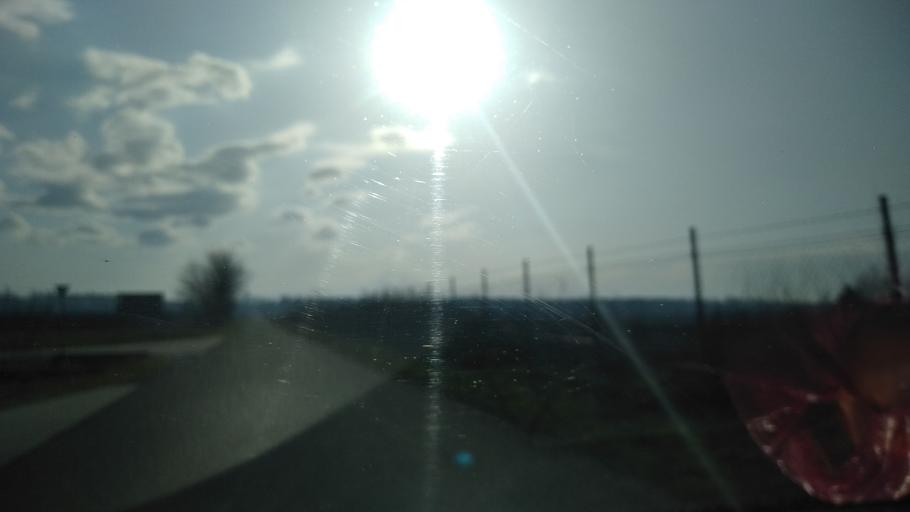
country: HU
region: Somogy
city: Barcs
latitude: 45.9719
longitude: 17.4972
